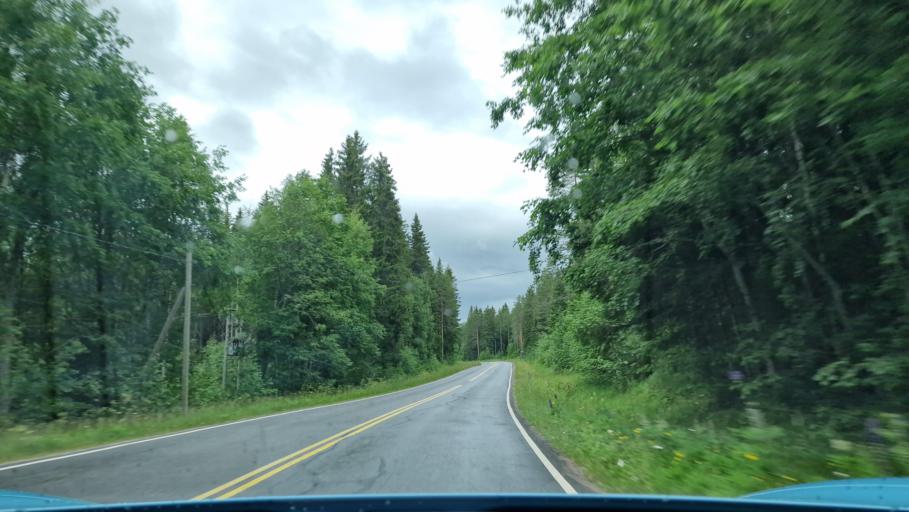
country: FI
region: Southern Ostrobothnia
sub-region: Jaerviseutu
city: Soini
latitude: 62.7623
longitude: 24.3862
